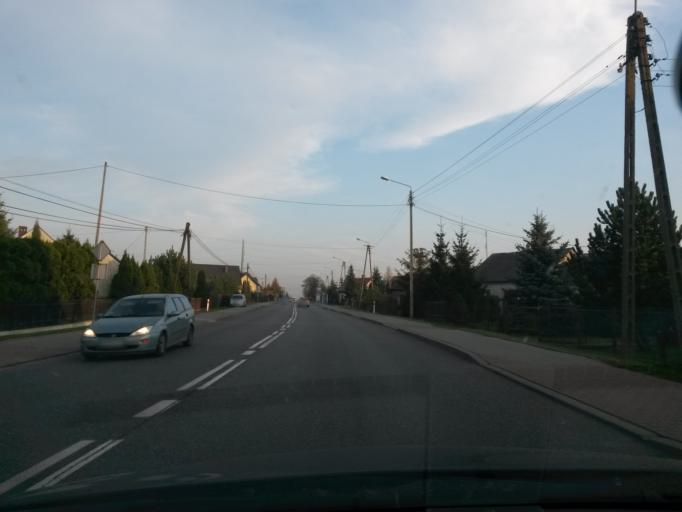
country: PL
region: Lodz Voivodeship
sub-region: Powiat wielunski
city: Wielun
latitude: 51.2310
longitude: 18.5422
